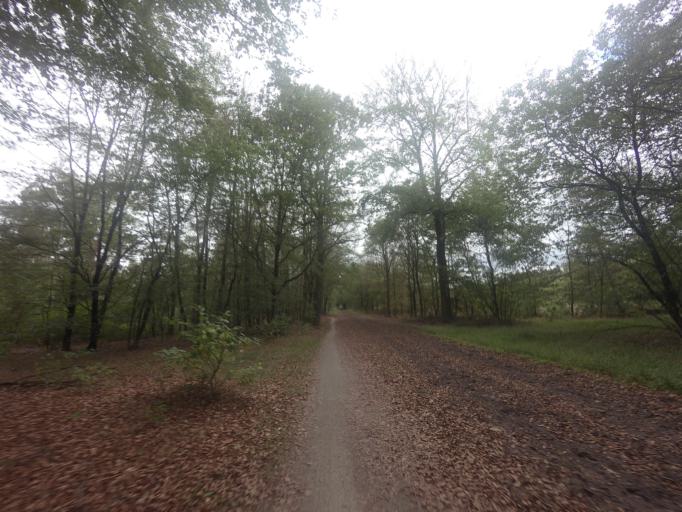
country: NL
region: Drenthe
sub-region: Gemeente Westerveld
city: Dwingeloo
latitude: 52.9297
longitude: 6.3184
